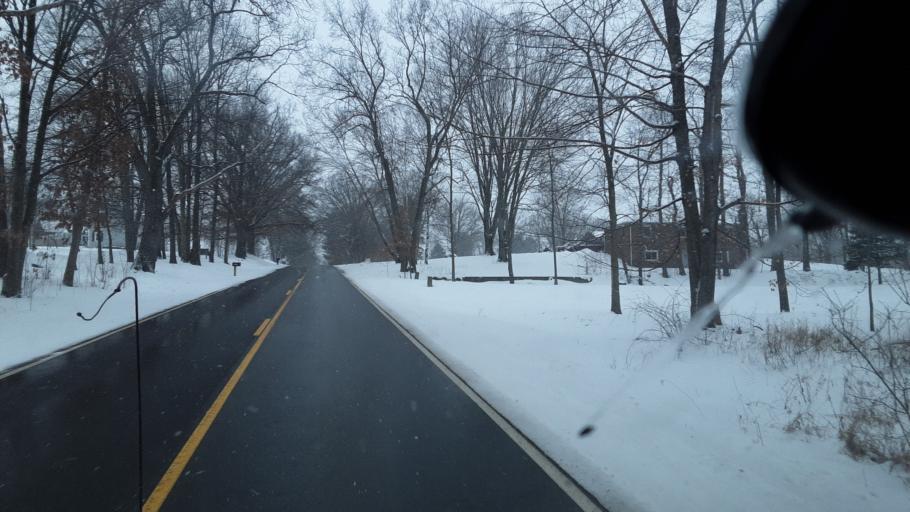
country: US
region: Michigan
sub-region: Ingham County
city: Leslie
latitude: 42.3850
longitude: -84.4433
